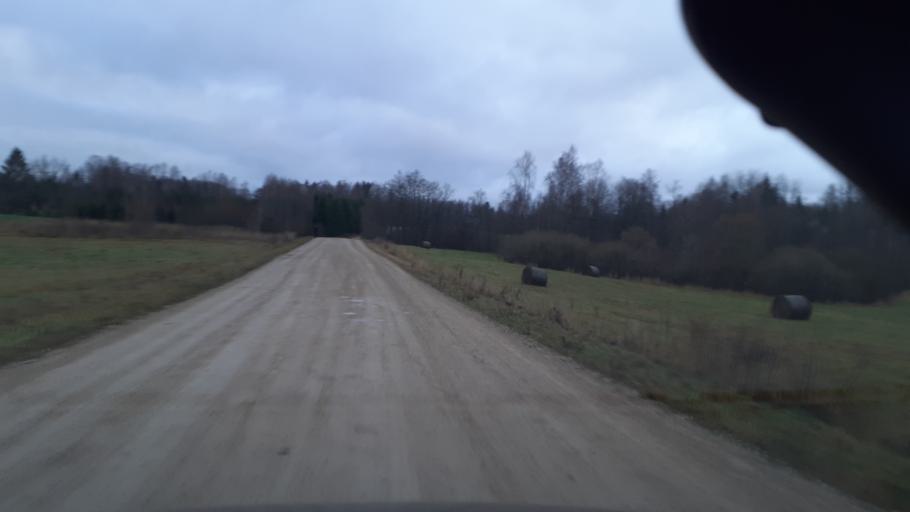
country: LV
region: Alsunga
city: Alsunga
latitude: 56.8845
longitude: 21.6948
